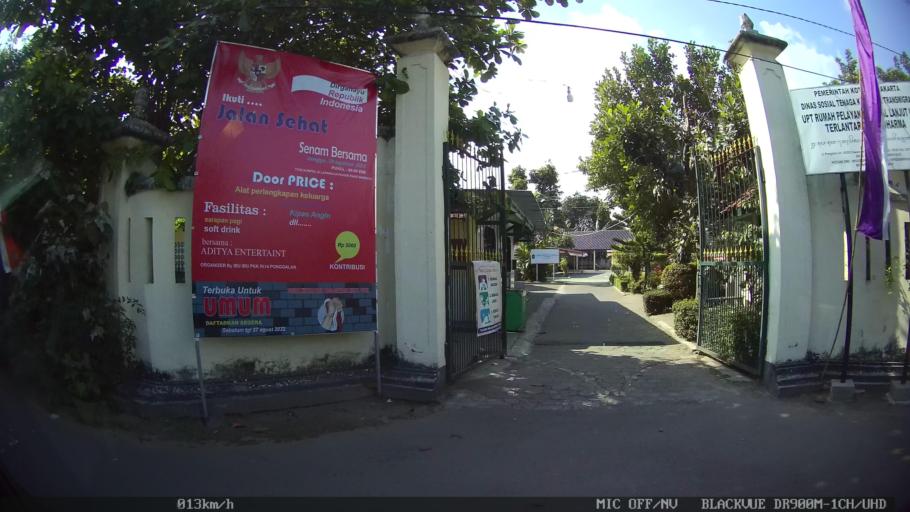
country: ID
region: Daerah Istimewa Yogyakarta
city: Yogyakarta
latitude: -7.8282
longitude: 110.3917
